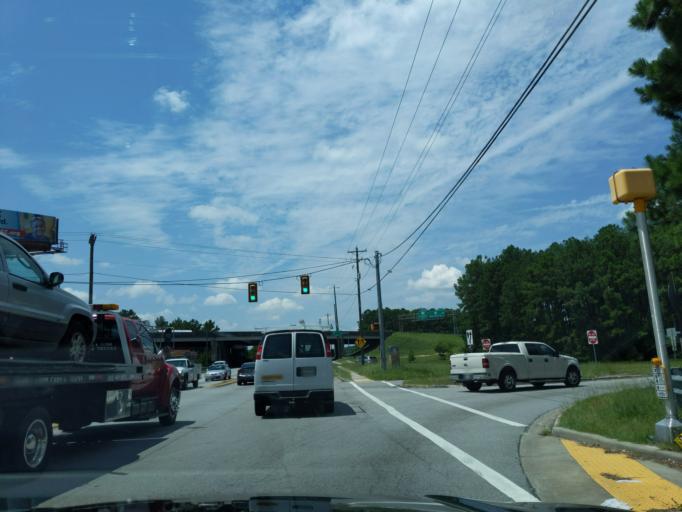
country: US
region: South Carolina
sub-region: Richland County
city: Dentsville
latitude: 34.0749
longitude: -80.9464
